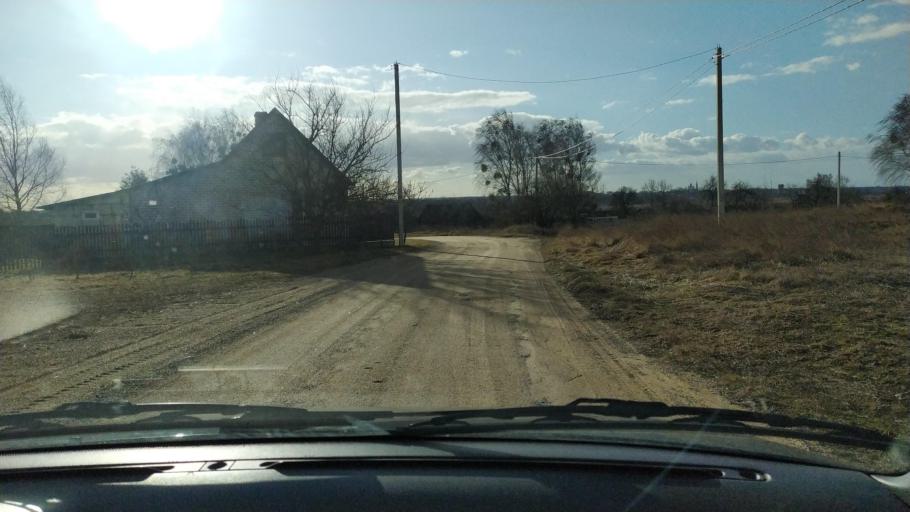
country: BY
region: Brest
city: Kamyanyets
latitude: 52.4240
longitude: 23.8224
